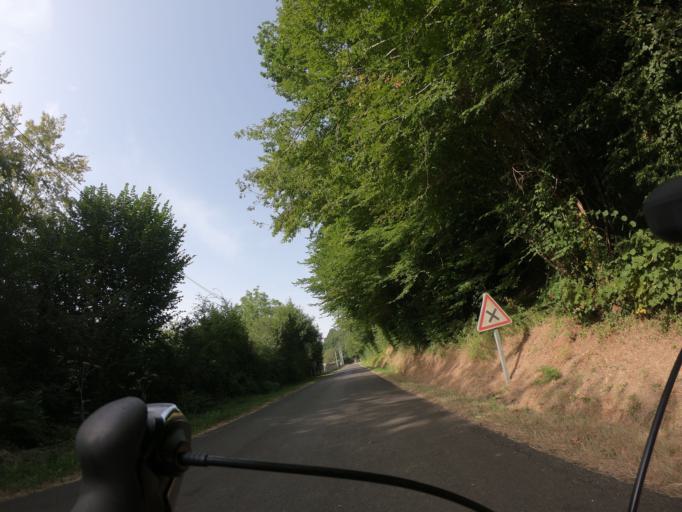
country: FR
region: Centre
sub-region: Departement d'Eure-et-Loir
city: Margon
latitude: 48.3446
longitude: 0.8270
